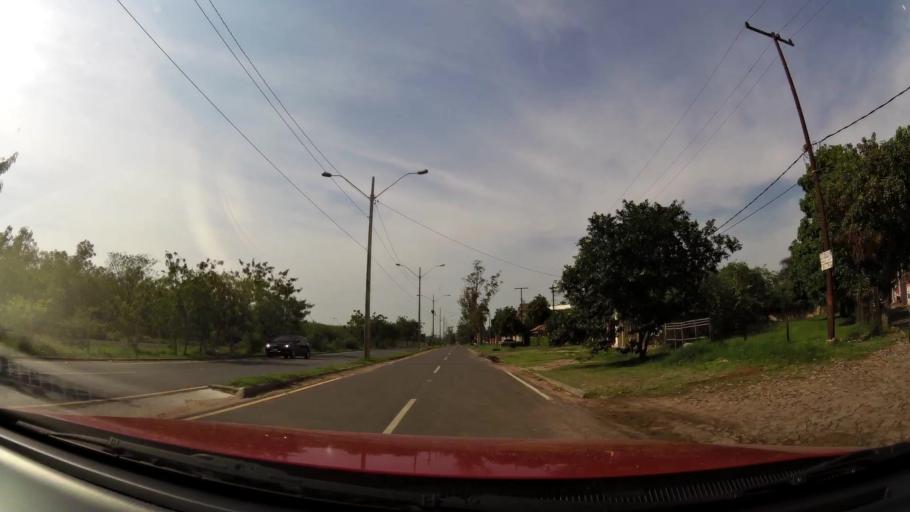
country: PY
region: Central
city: Fernando de la Mora
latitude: -25.2580
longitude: -57.5489
